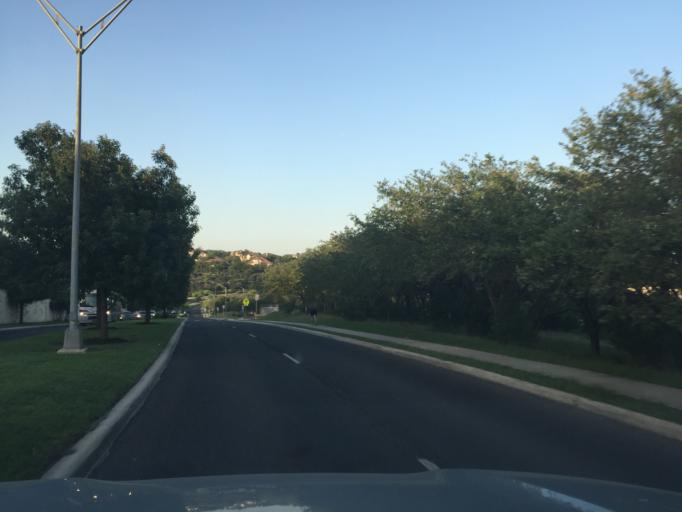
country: US
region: Texas
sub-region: Bexar County
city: Hollywood Park
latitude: 29.6378
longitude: -98.4709
